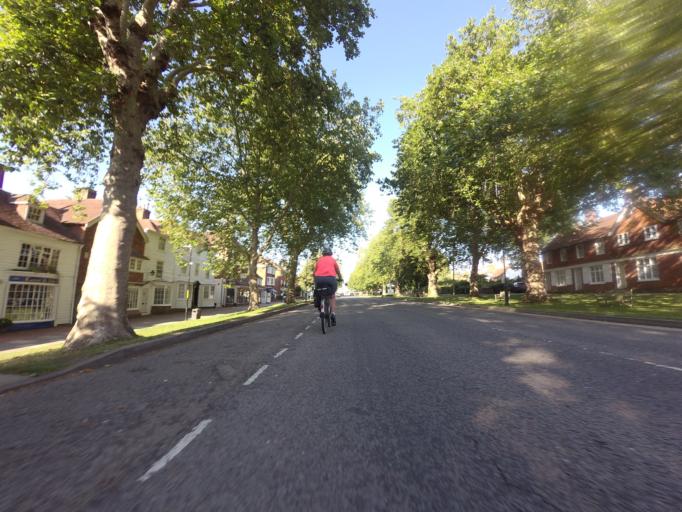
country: GB
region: England
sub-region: Kent
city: Tenterden
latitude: 51.0670
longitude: 0.6832
